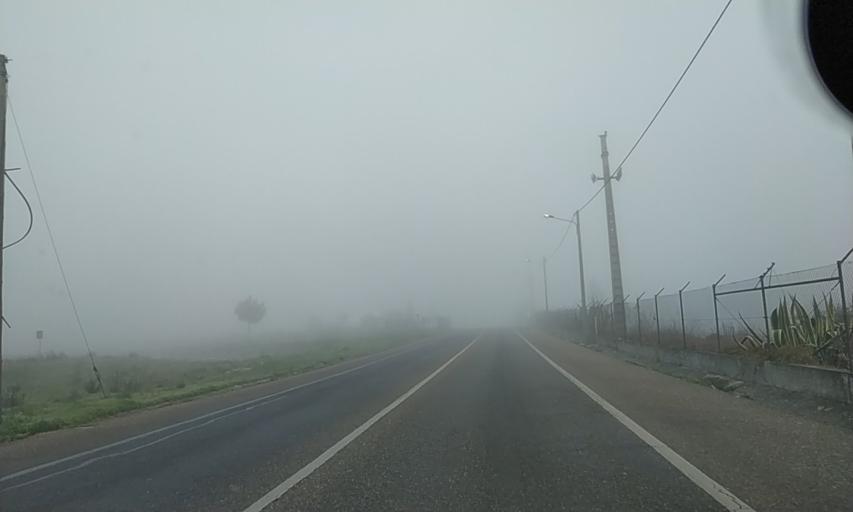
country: PT
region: Setubal
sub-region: Palmela
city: Pinhal Novo
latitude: 38.6168
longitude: -8.9136
